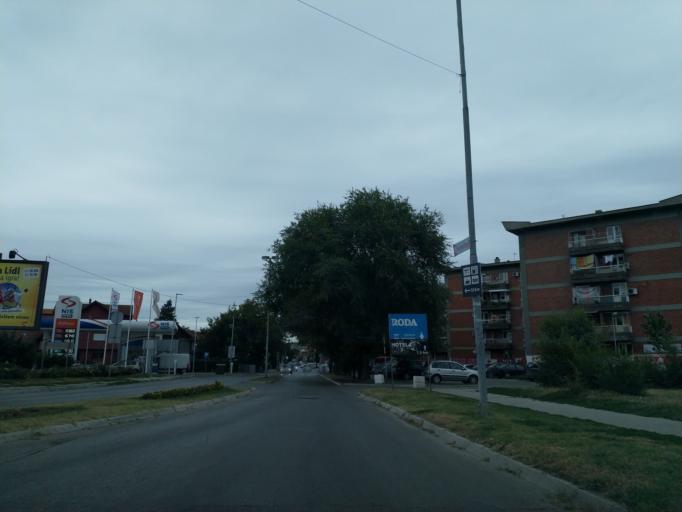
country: RS
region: Central Serbia
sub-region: Pomoravski Okrug
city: Jagodina
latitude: 43.9859
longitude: 21.2500
